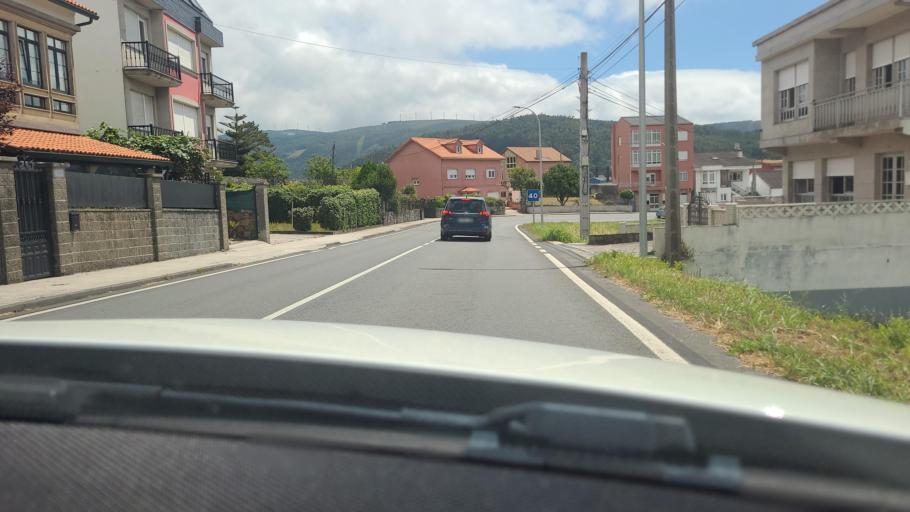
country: ES
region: Galicia
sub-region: Provincia da Coruna
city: Cee
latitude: 42.9479
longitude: -9.1803
